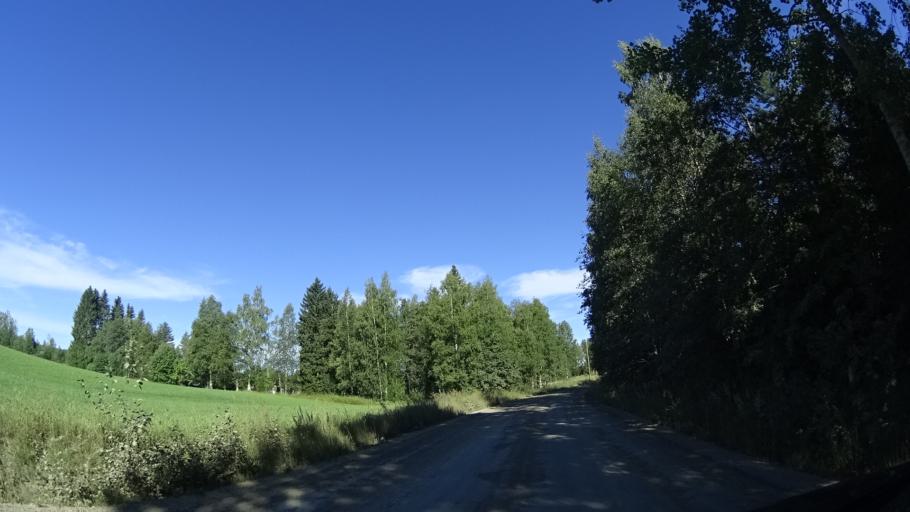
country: FI
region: Central Finland
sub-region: Jyvaeskylae
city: Petaejaevesi
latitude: 62.3539
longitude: 25.3255
